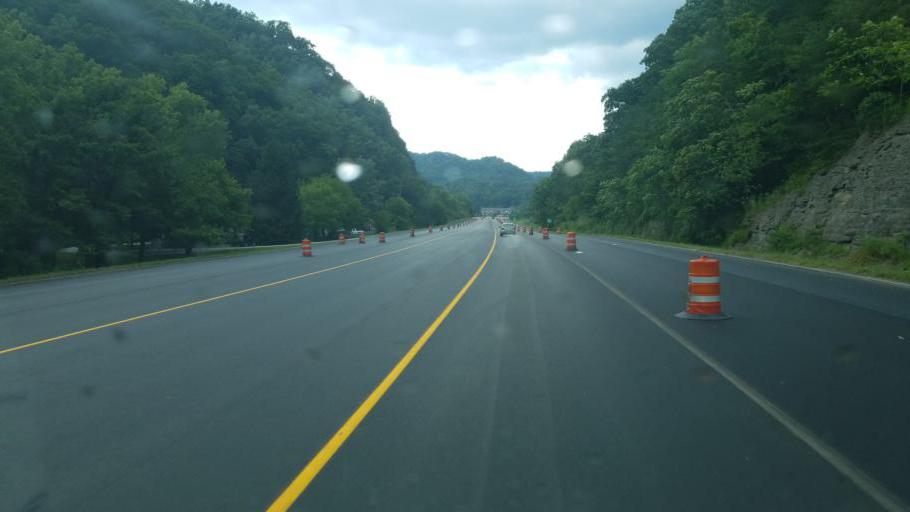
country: US
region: Kentucky
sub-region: Pike County
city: Pikeville
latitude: 37.5073
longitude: -82.5218
